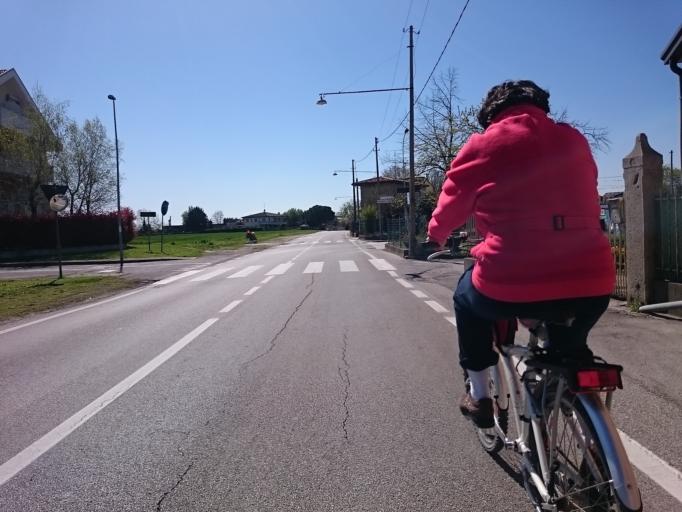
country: IT
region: Veneto
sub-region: Provincia di Padova
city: Ponte San Nicolo
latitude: 45.3748
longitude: 11.9042
